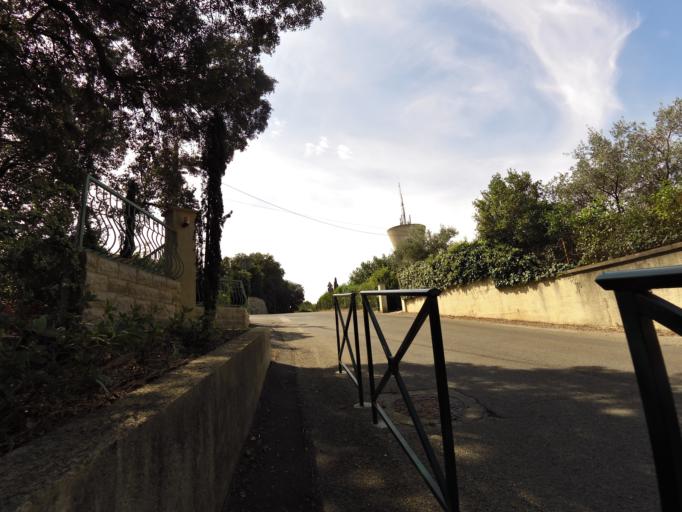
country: FR
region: Languedoc-Roussillon
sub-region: Departement du Gard
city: Mus
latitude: 43.7419
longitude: 4.2035
